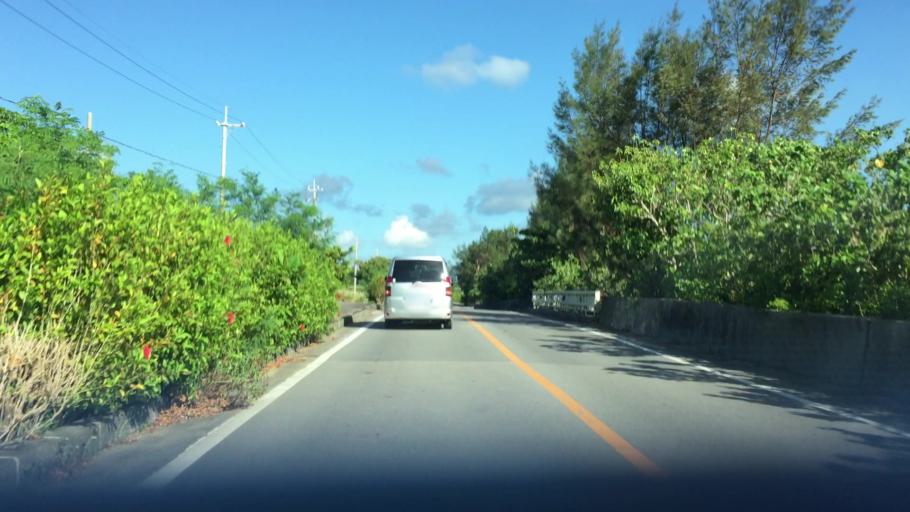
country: JP
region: Okinawa
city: Ishigaki
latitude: 24.4262
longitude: 124.1274
